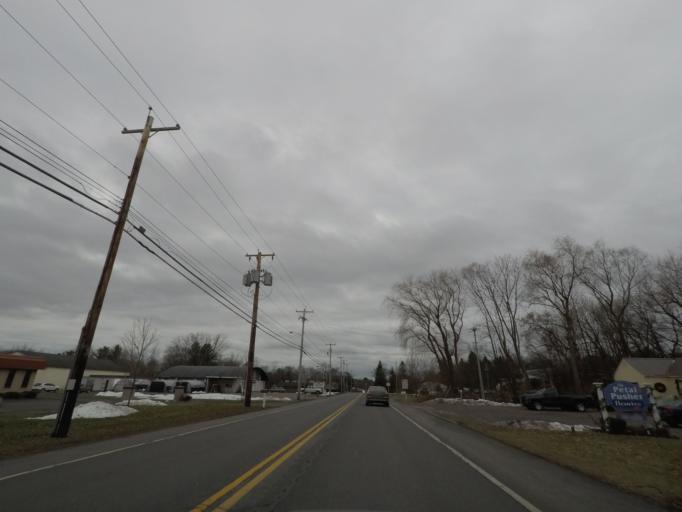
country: US
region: New York
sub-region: Schenectady County
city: East Glenville
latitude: 42.9033
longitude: -73.9041
